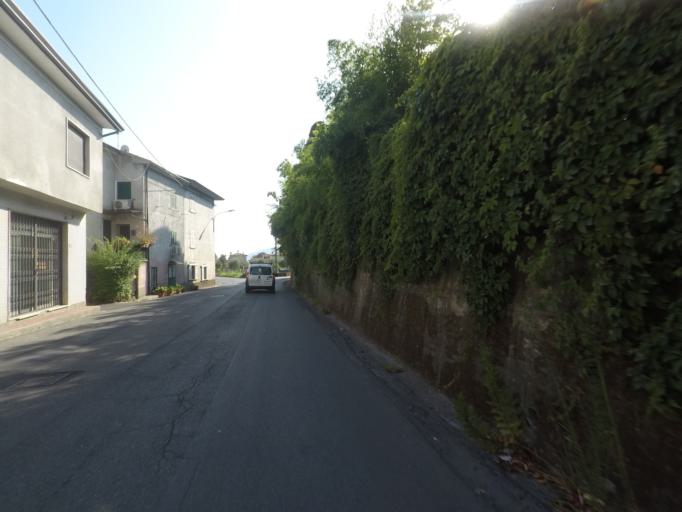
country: IT
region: Liguria
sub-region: Provincia di La Spezia
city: Casano-Dogana-Isola
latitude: 44.0806
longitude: 10.0338
